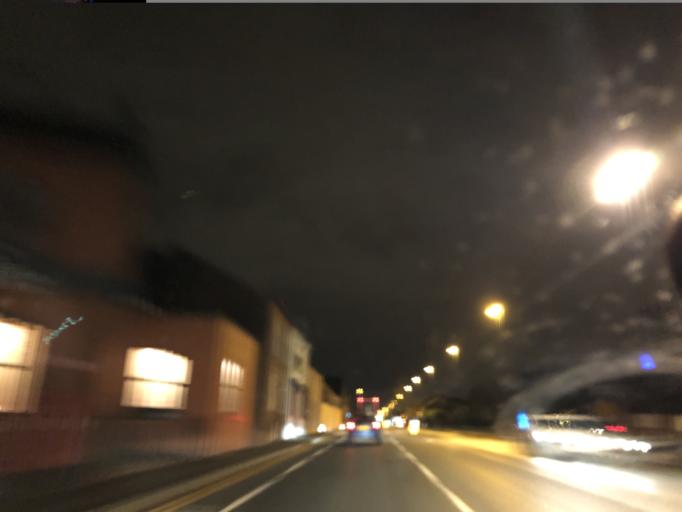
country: GB
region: England
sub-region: Manchester
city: Failsworth
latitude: 53.5120
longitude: -2.1552
